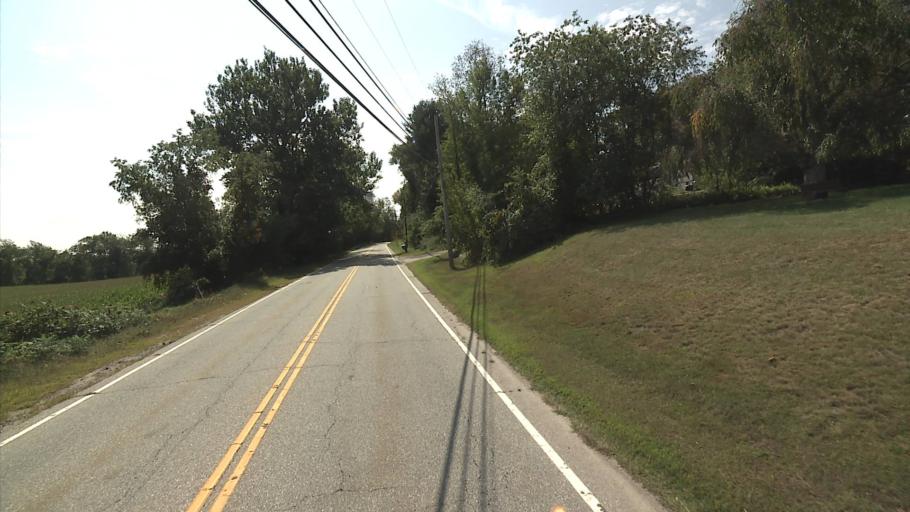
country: US
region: Connecticut
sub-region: Windham County
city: Plainfield Village
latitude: 41.6689
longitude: -71.9721
